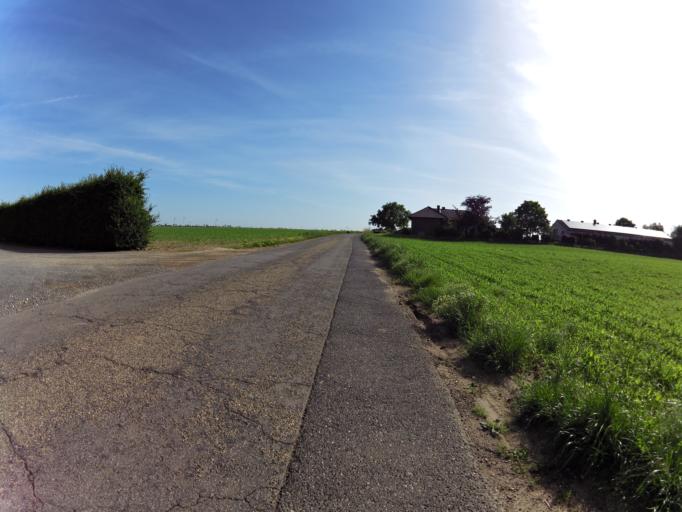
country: DE
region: North Rhine-Westphalia
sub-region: Regierungsbezirk Koln
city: Gangelt
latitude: 51.0084
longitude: 5.9752
